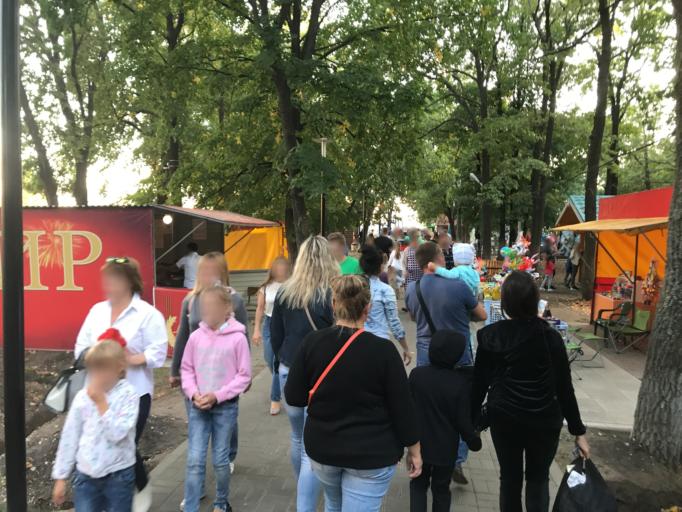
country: RU
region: Ulyanovsk
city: Mirnyy
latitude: 54.3925
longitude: 48.5759
